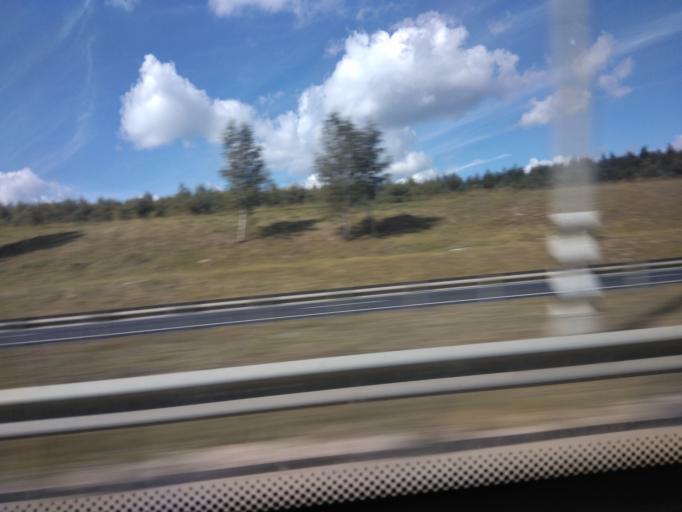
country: RU
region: Tula
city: Zaokskiy
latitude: 54.7479
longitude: 37.4919
